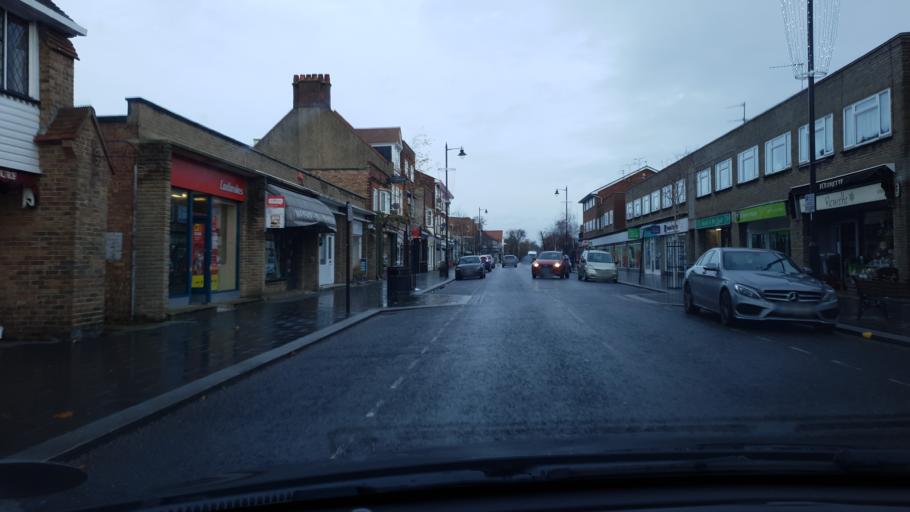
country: GB
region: England
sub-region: Essex
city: Frinton-on-Sea
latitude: 51.8332
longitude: 1.2451
